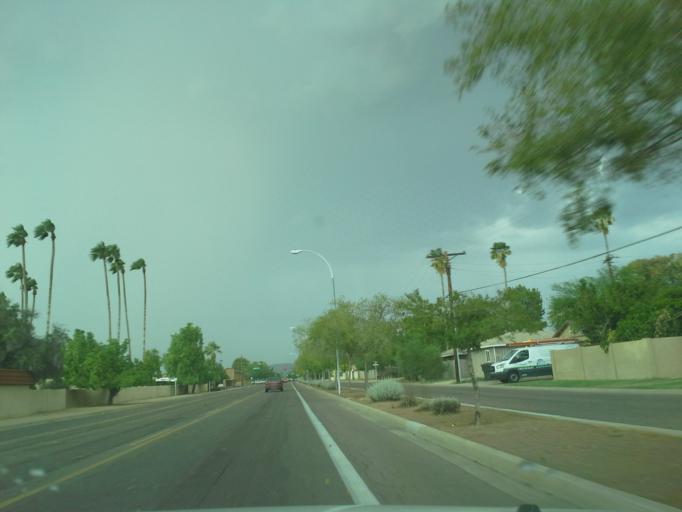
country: US
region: Arizona
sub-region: Maricopa County
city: Phoenix
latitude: 33.5140
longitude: -112.0912
